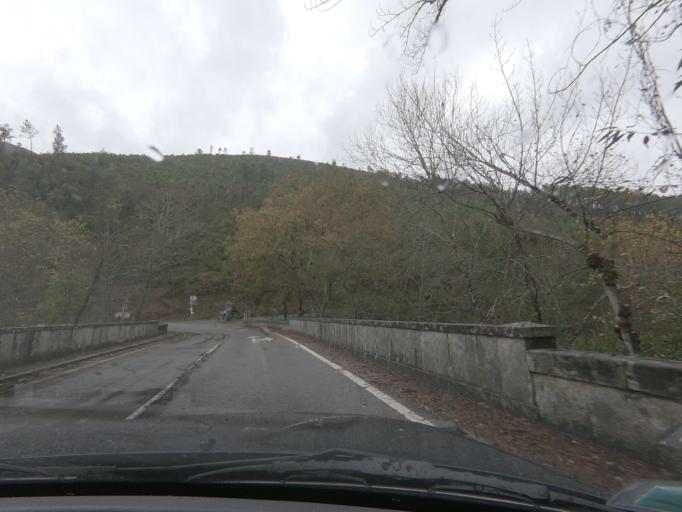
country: PT
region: Vila Real
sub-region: Mondim de Basto
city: Mondim de Basto
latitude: 41.3548
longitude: -7.8811
